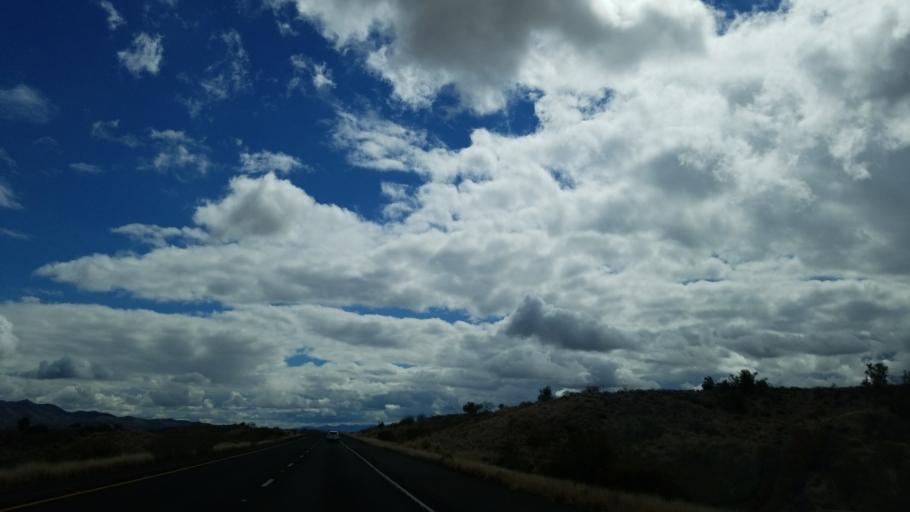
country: US
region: Arizona
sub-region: Mohave County
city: Kingman
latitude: 35.0760
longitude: -113.6660
